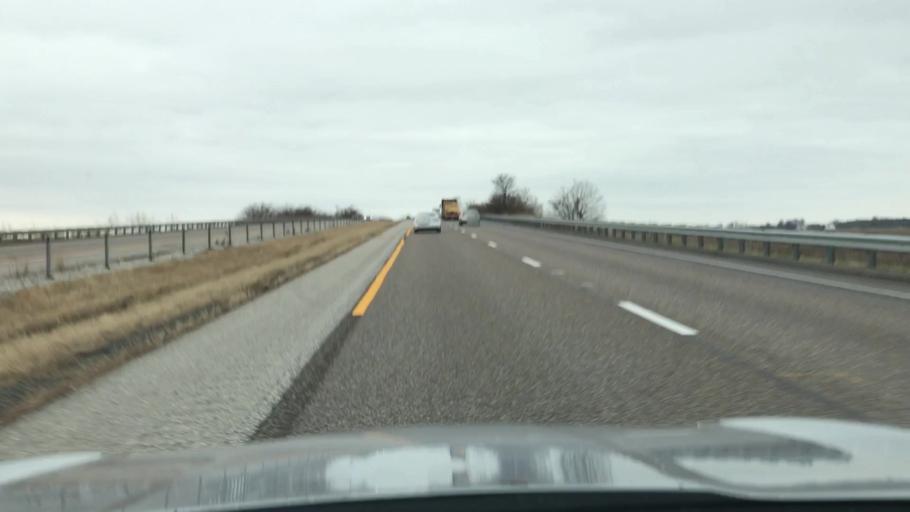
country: US
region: Illinois
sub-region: Madison County
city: Edwardsville
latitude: 38.8279
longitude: -89.8811
